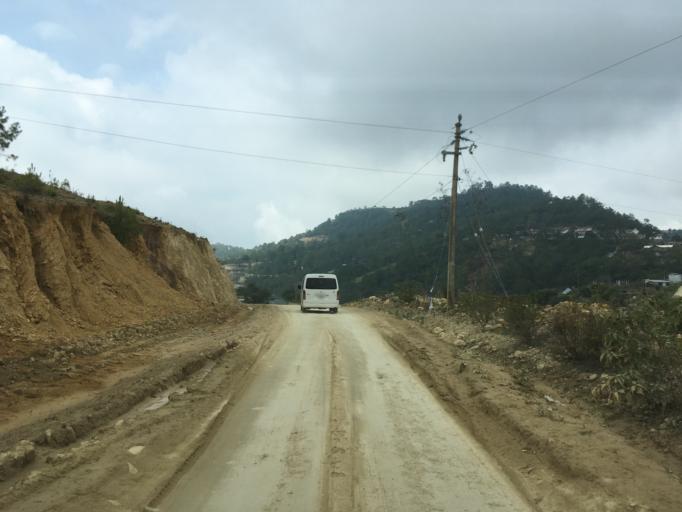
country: MX
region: Oaxaca
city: Santiago Tilantongo
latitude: 17.1986
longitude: -97.2812
